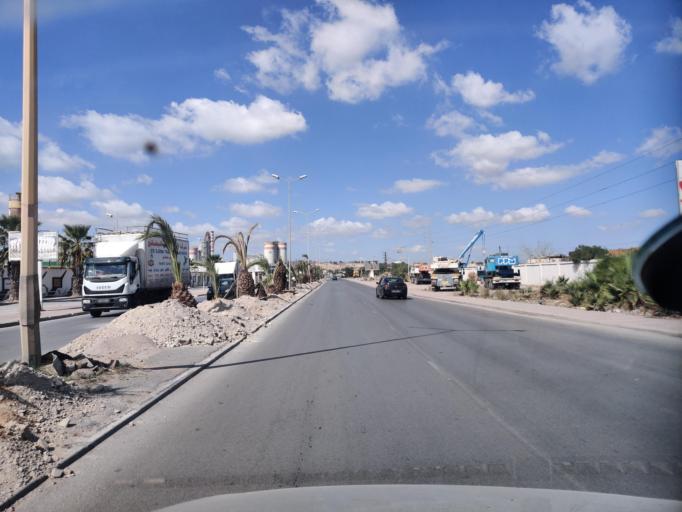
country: TN
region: Bin 'Arus
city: Ben Arous
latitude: 36.7762
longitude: 10.2125
